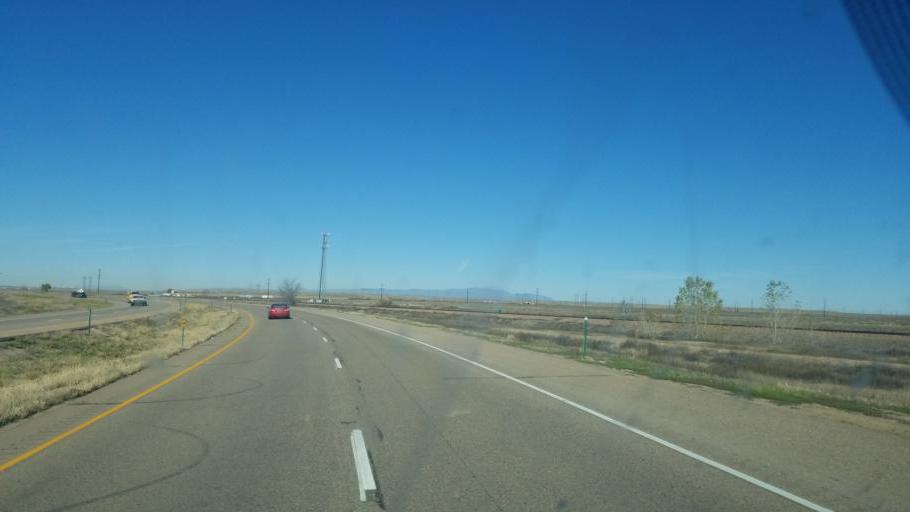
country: US
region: Colorado
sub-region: Pueblo County
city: Pueblo
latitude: 38.2666
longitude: -104.3741
